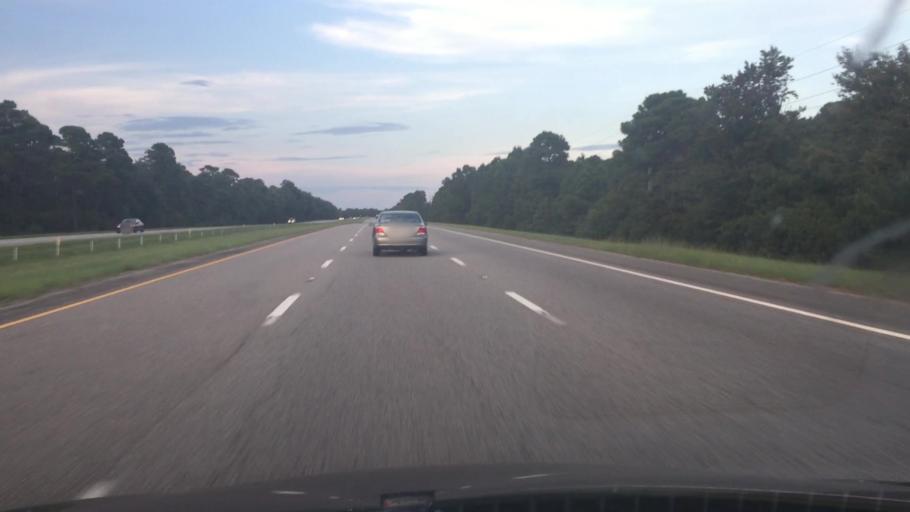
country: US
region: South Carolina
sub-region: Horry County
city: Forestbrook
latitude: 33.7472
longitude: -78.9116
